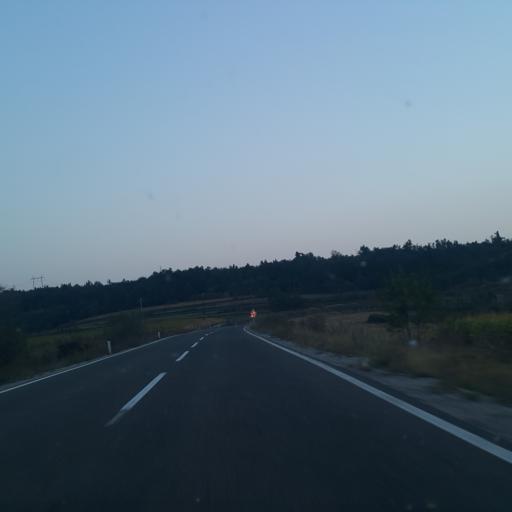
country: RS
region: Central Serbia
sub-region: Nisavski Okrug
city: Svrljig
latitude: 43.4481
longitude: 22.1712
